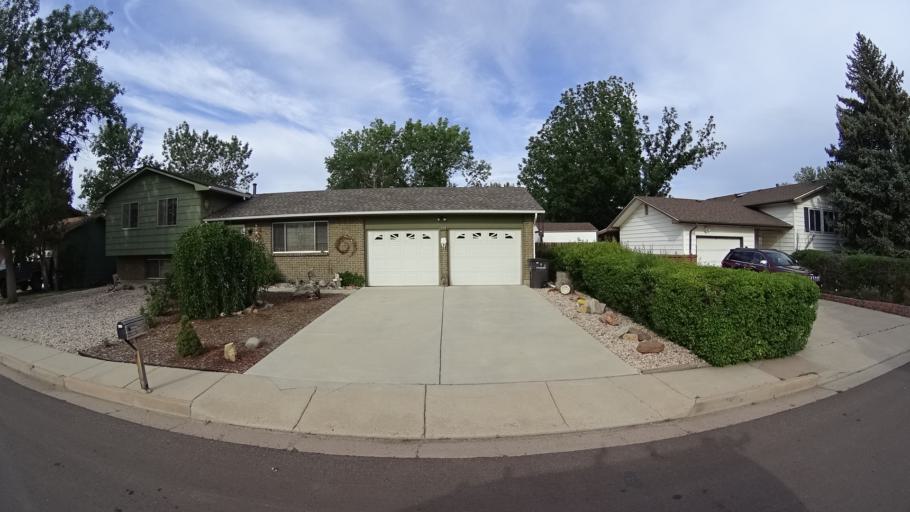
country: US
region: Colorado
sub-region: El Paso County
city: Security-Widefield
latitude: 38.7315
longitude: -104.6930
